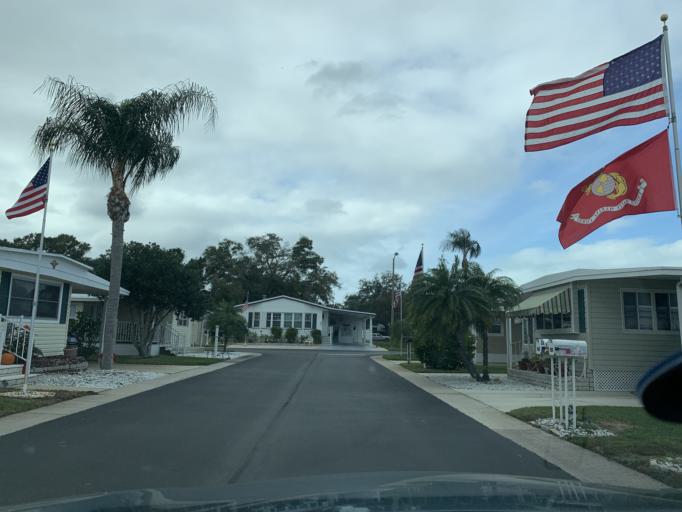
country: US
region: Florida
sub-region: Pinellas County
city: Ridgecrest
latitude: 27.8851
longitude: -82.7926
